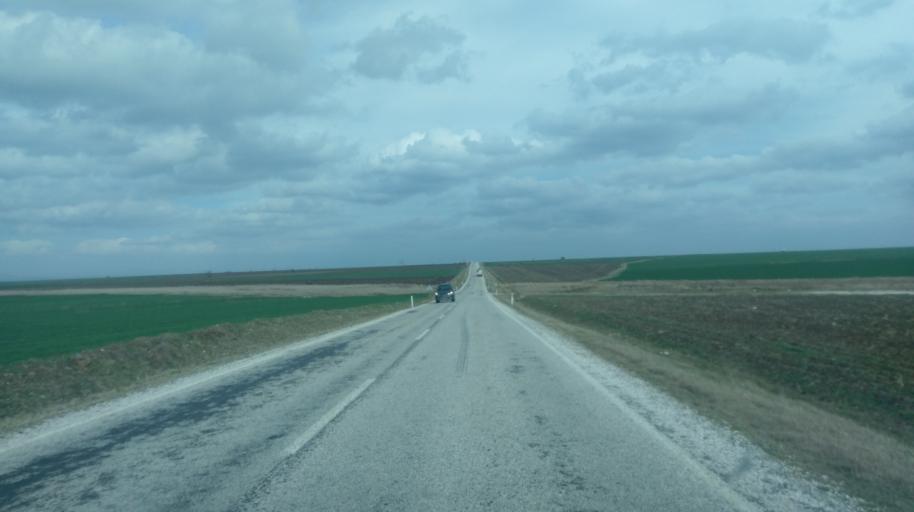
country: TR
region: Edirne
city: Haskoy
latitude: 41.6501
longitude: 26.8884
